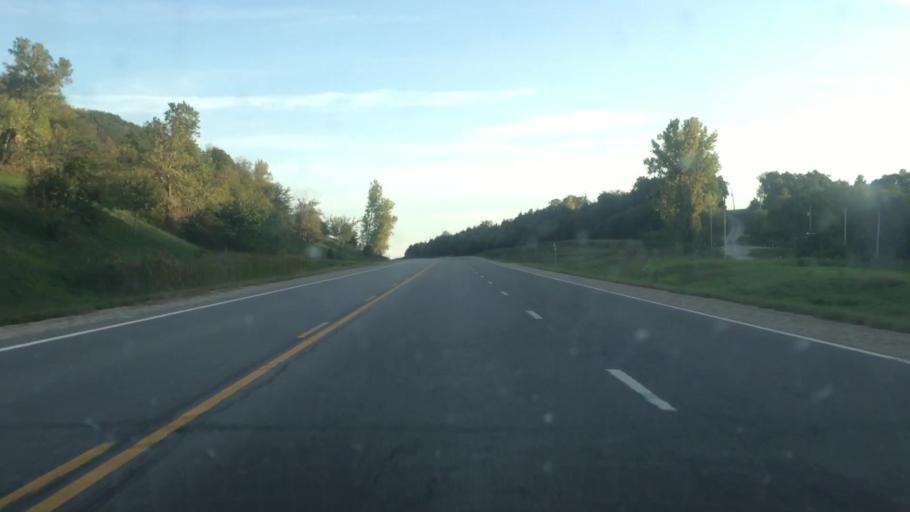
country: US
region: Kansas
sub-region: Atchison County
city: Atchison
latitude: 39.4938
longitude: -95.1318
